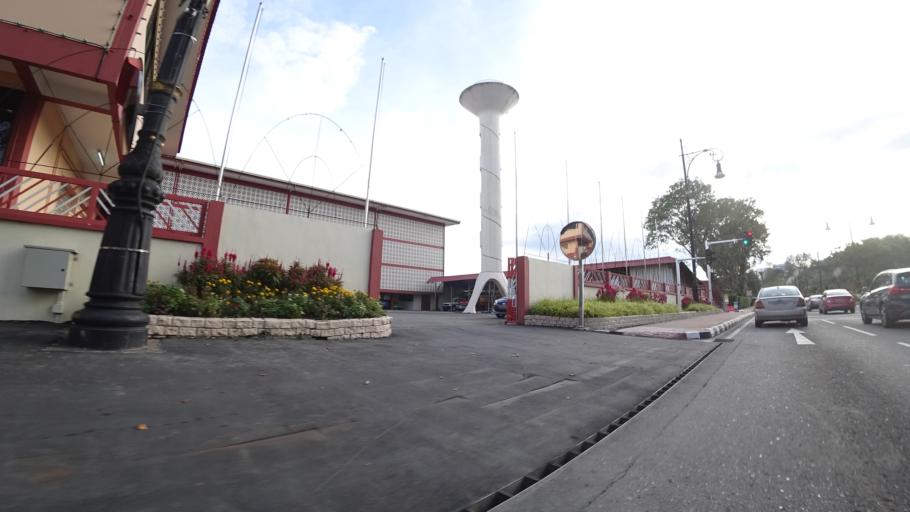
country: BN
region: Brunei and Muara
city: Bandar Seri Begawan
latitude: 4.8941
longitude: 114.9370
